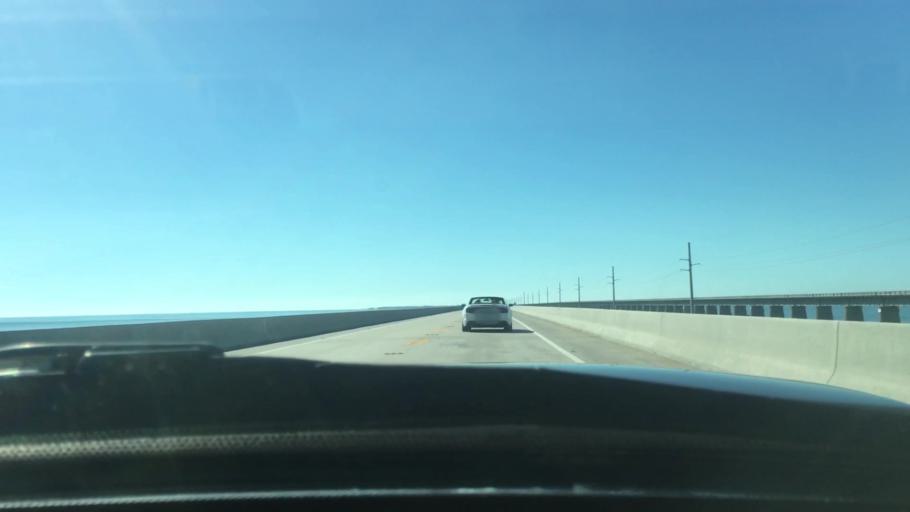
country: US
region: Florida
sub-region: Monroe County
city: Marathon
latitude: 24.6959
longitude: -81.1791
